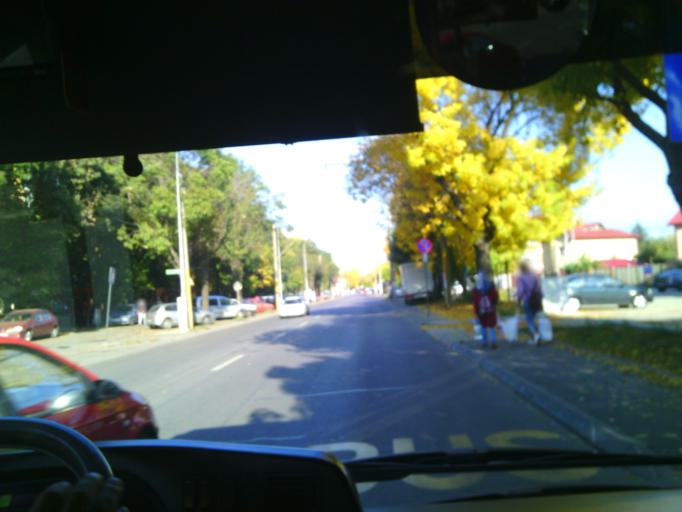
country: RO
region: Ilfov
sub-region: Comuna Popesti-Leordeni
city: Popesti-Leordeni
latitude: 44.3782
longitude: 26.1243
